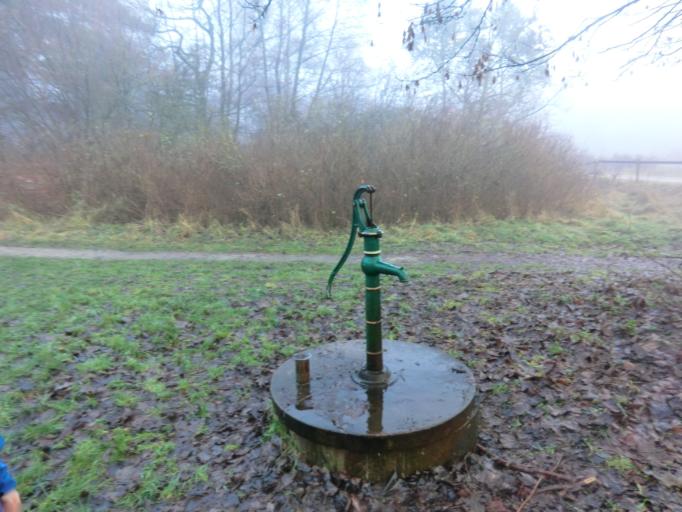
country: SE
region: Skane
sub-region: Lunds Kommun
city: Veberod
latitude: 55.6908
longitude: 13.4948
